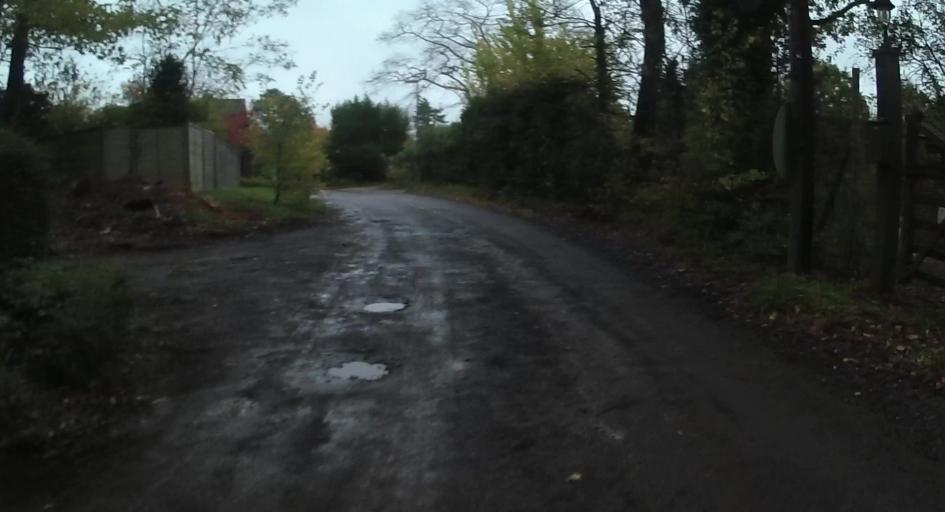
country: GB
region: England
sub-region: Surrey
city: Farnham
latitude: 51.2199
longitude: -0.8068
